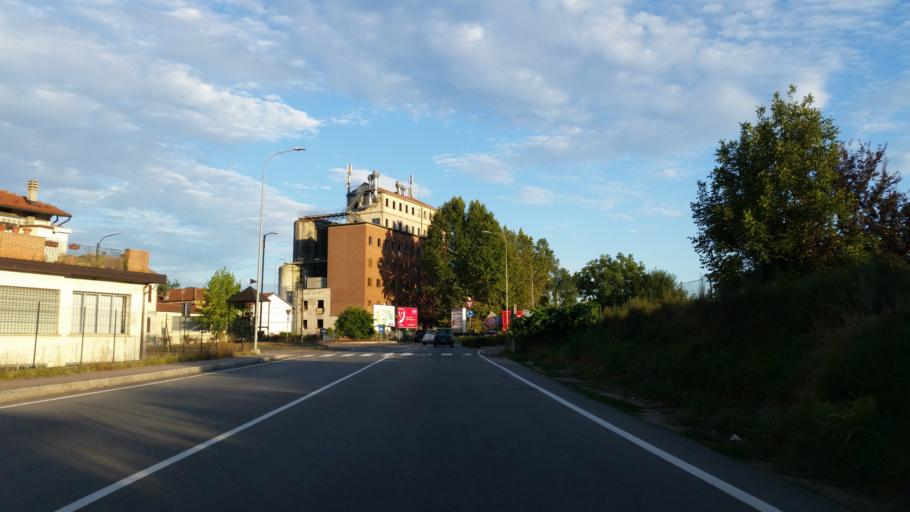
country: IT
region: Piedmont
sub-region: Provincia di Asti
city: Asti
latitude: 44.8874
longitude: 8.2110
